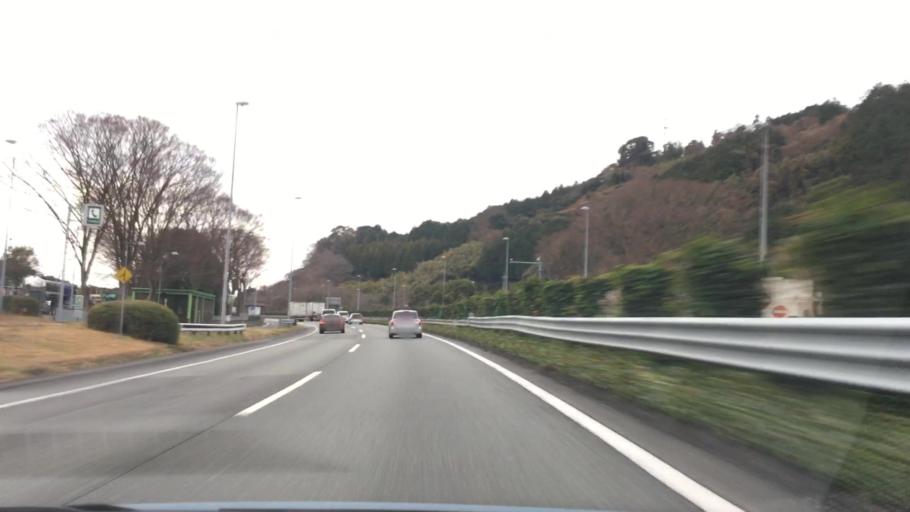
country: JP
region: Shizuoka
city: Fujinomiya
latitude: 35.1585
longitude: 138.6183
